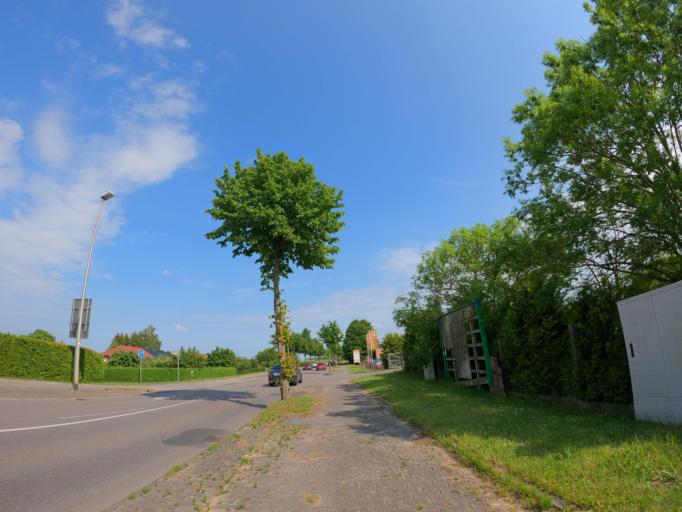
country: DE
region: Mecklenburg-Vorpommern
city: Stralsund
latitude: 54.2890
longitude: 13.0542
